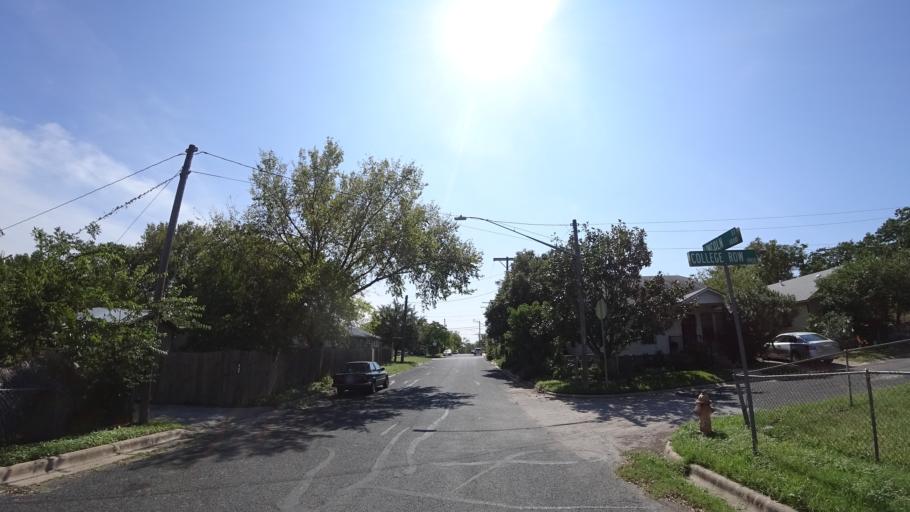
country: US
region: Texas
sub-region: Travis County
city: Austin
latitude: 30.2653
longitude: -97.7194
